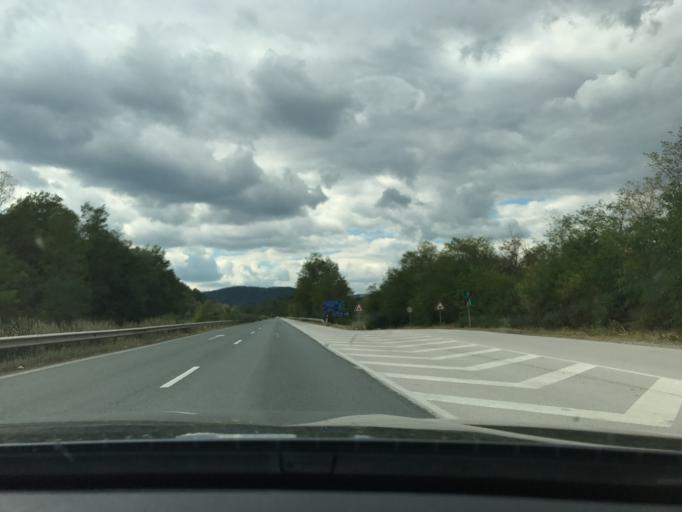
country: BG
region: Sofiya
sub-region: Obshtina Botevgrad
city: Botevgrad
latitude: 42.8929
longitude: 23.8312
